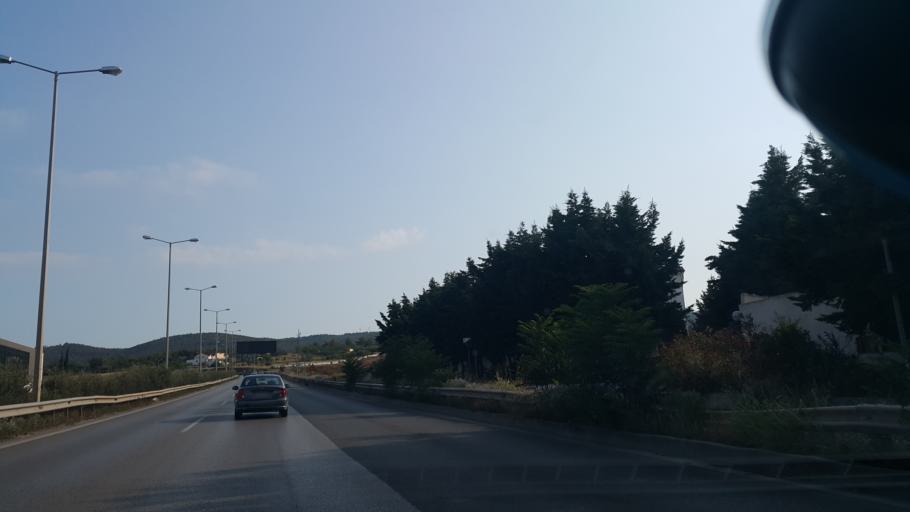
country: GR
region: Central Macedonia
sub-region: Nomos Thessalonikis
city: Pylaia
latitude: 40.6070
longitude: 22.9995
